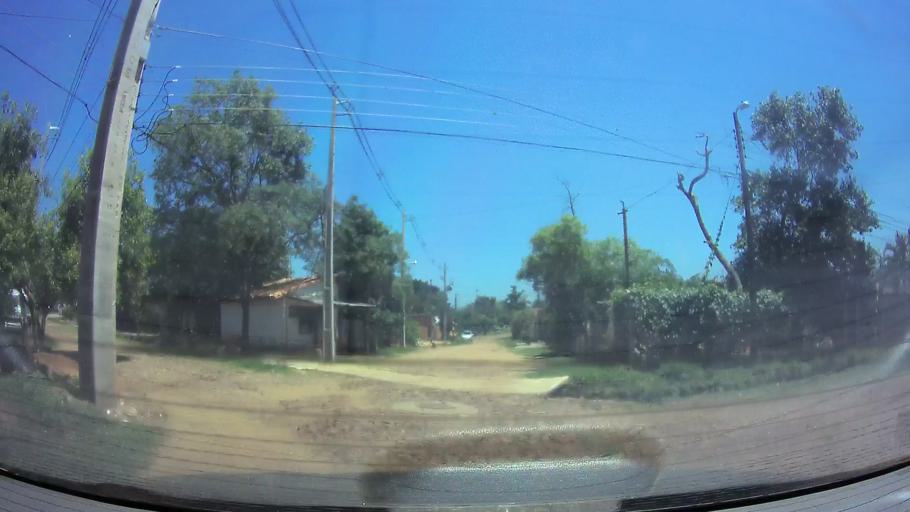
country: PY
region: Central
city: San Lorenzo
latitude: -25.3475
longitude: -57.4903
